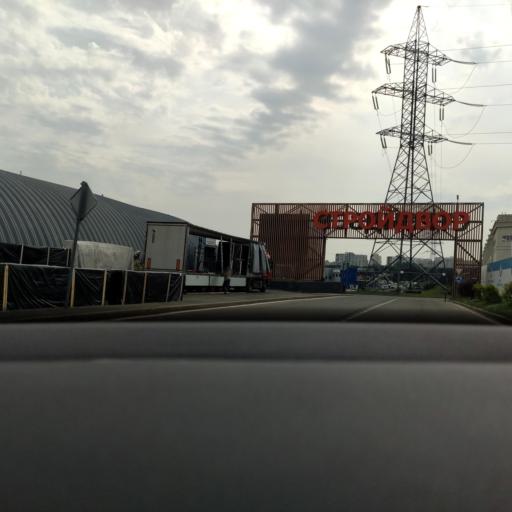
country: RU
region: Moscow
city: Vatutino
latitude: 55.9000
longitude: 37.6778
